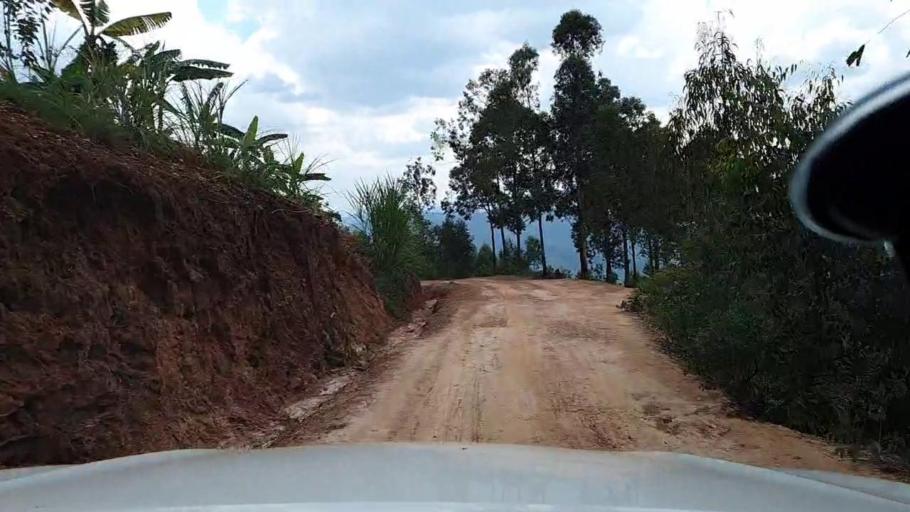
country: RW
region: Southern Province
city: Gitarama
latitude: -1.8406
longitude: 29.8228
